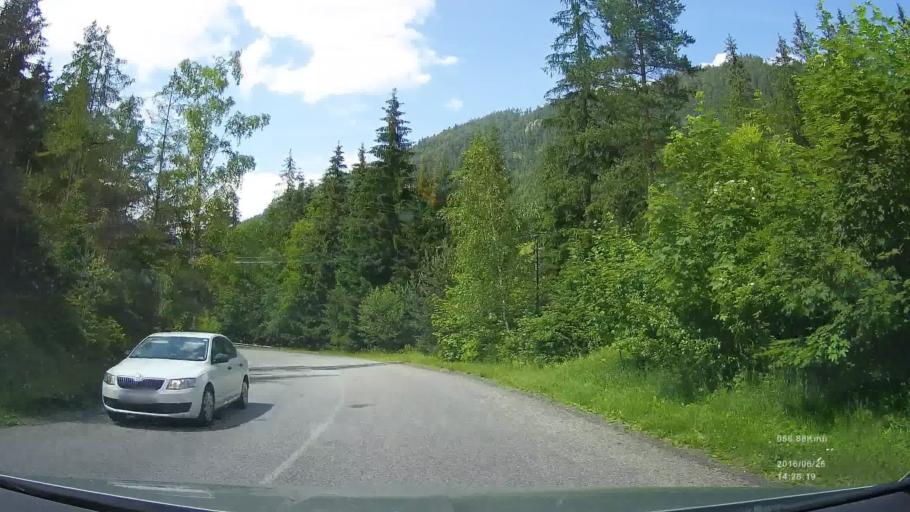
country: SK
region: Zilinsky
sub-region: Okres Zilina
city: Liptovsky Hradok
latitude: 48.9770
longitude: 19.7775
